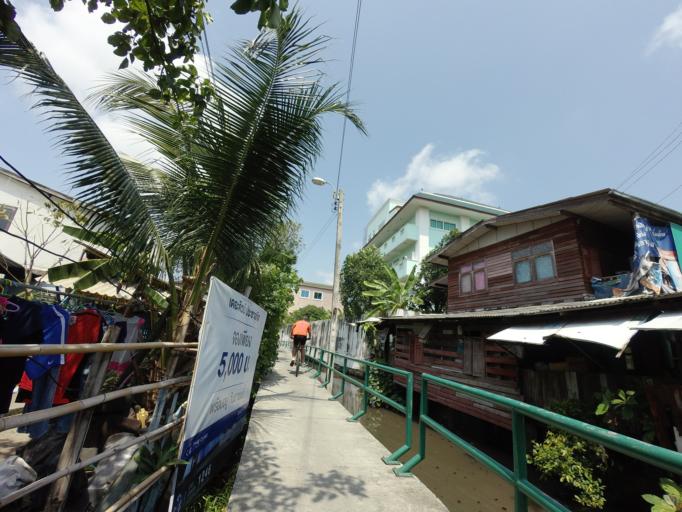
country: TH
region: Bangkok
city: Thung Khru
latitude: 13.6525
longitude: 100.5023
